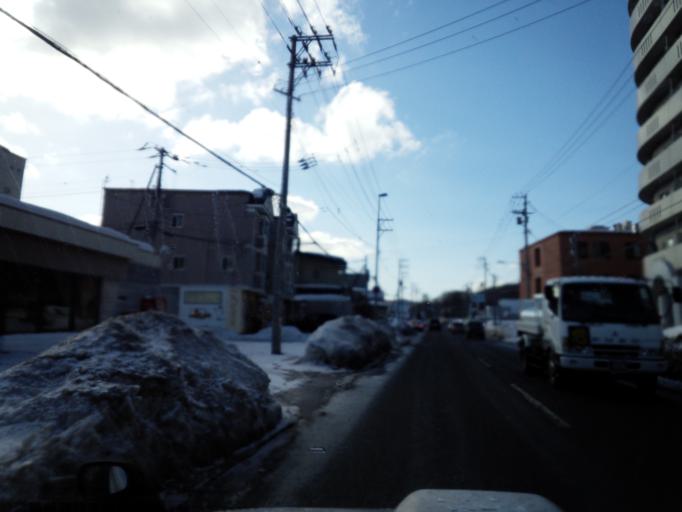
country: JP
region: Hokkaido
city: Sapporo
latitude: 42.9559
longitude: 141.3441
